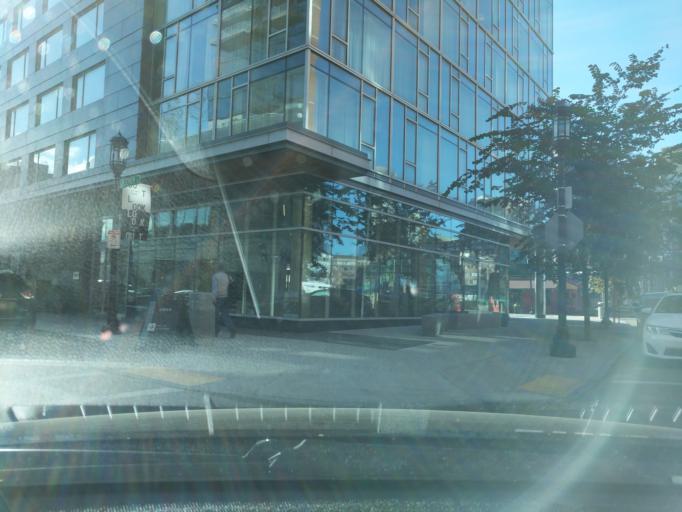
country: US
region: Massachusetts
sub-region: Suffolk County
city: Boston
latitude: 42.3540
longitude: -71.0479
